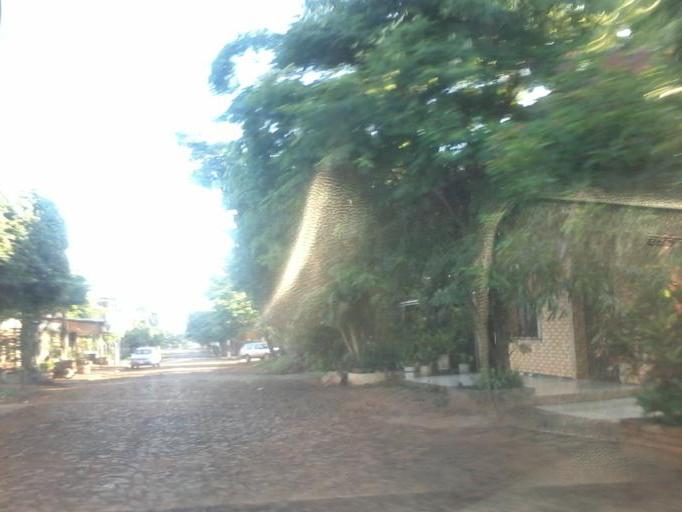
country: PY
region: Alto Parana
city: Ciudad del Este
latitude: -25.4359
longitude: -54.6440
